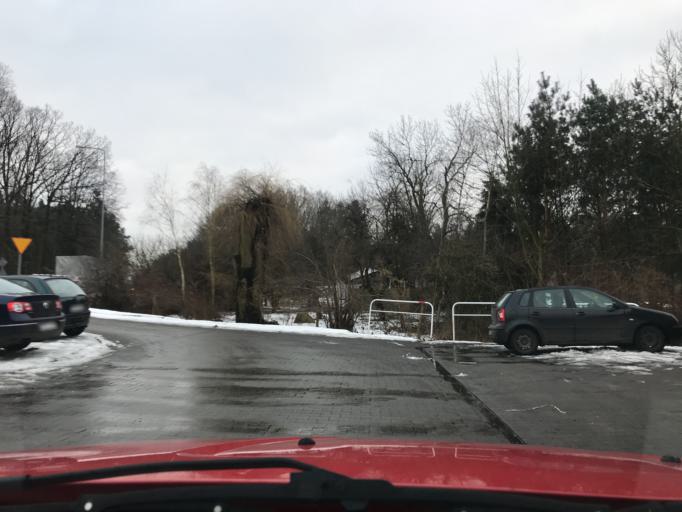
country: PL
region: Greater Poland Voivodeship
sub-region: Powiat pleszewski
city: Goluchow
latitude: 51.8473
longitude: 17.9377
